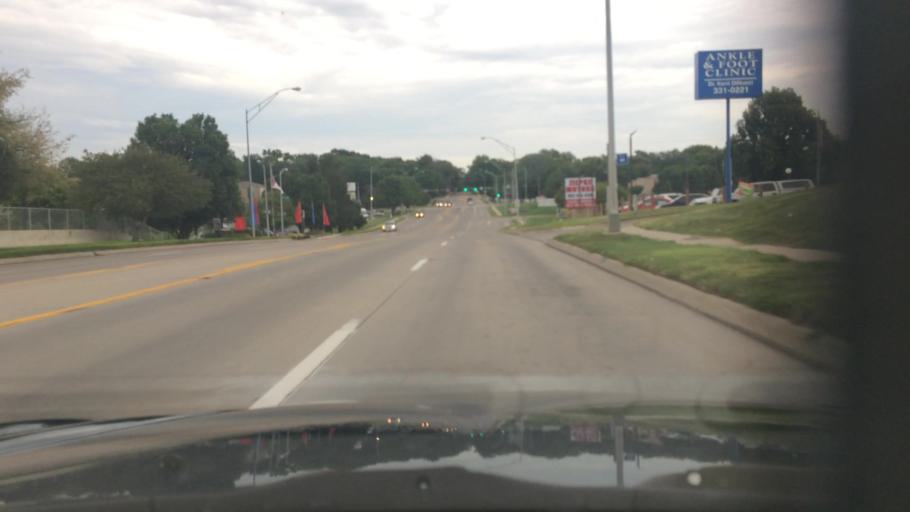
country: US
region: Nebraska
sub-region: Douglas County
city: Ralston
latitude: 41.2052
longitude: -96.0465
